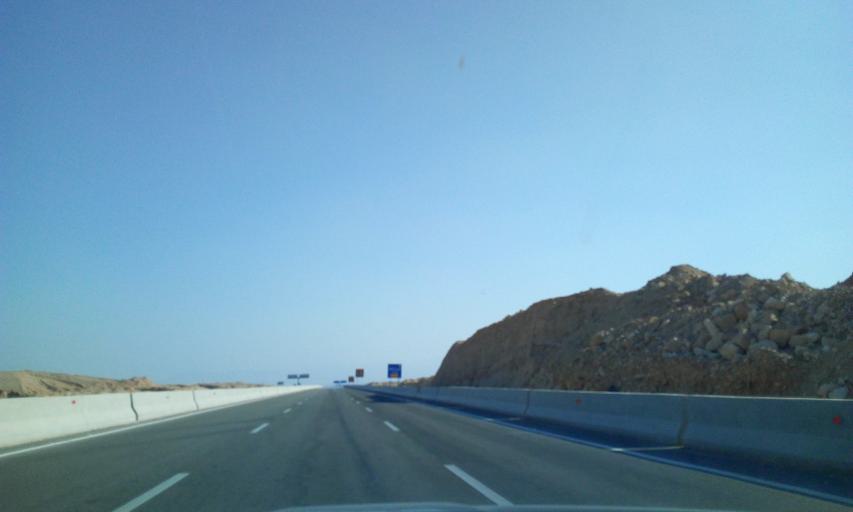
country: EG
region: As Suways
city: Ain Sukhna
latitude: 29.2920
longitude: 32.4672
